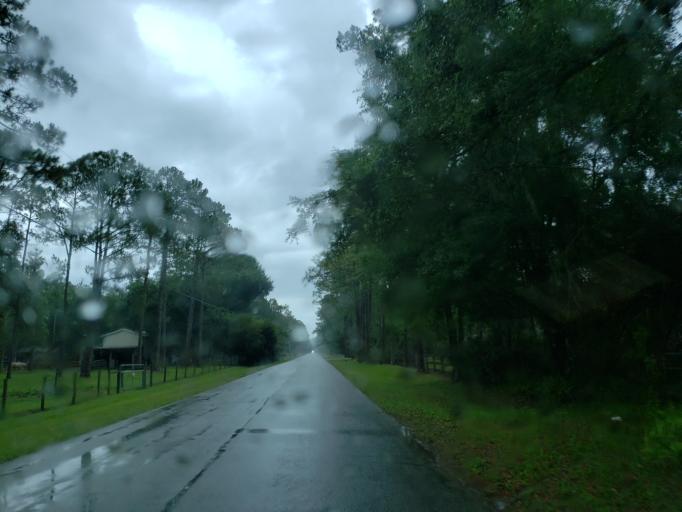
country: US
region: Florida
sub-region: Pasco County
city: Wesley Chapel
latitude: 28.2730
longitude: -82.3623
